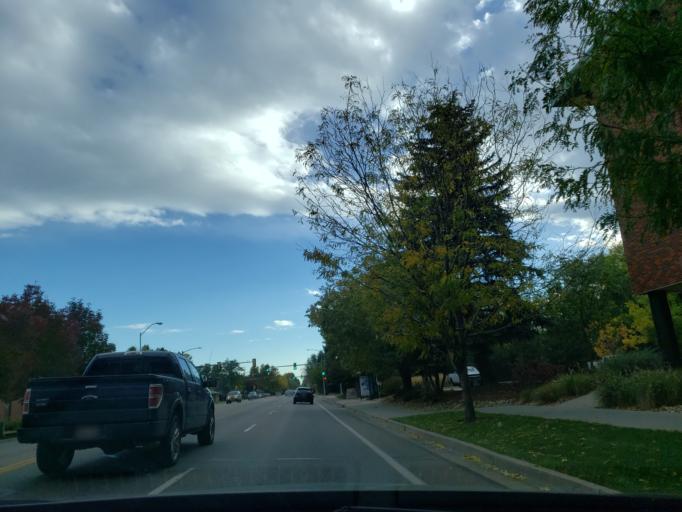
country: US
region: Colorado
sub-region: Larimer County
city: Fort Collins
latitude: 40.5721
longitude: -105.0580
